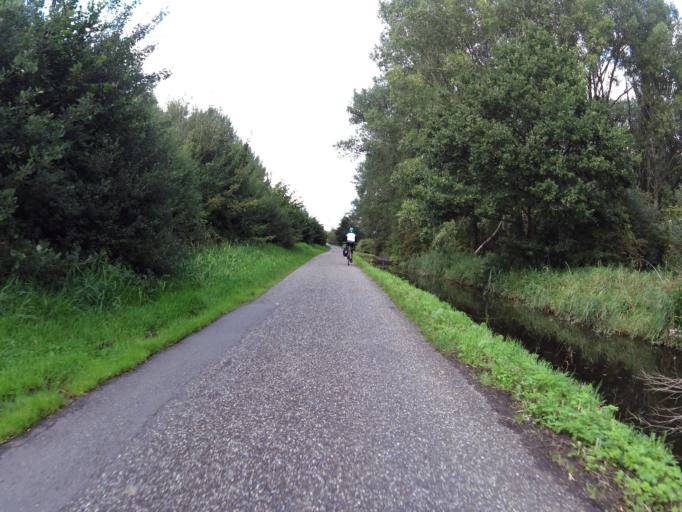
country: NL
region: Utrecht
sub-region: Stichtse Vecht
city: Breukelen
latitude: 52.1715
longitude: 5.0229
